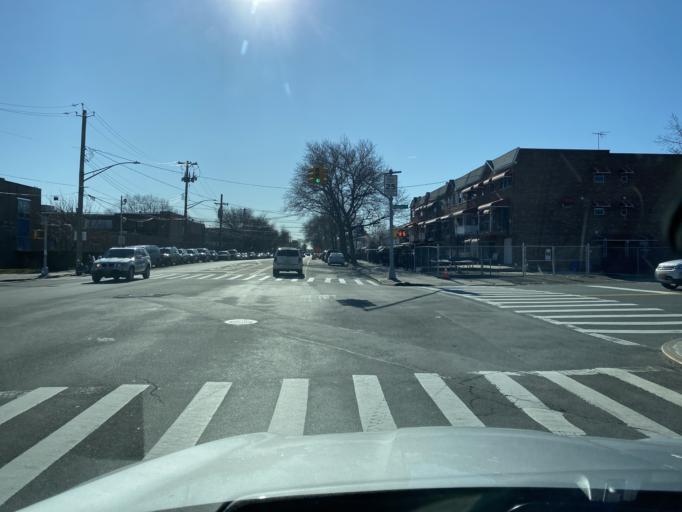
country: US
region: New York
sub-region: Bronx
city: The Bronx
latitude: 40.8179
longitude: -73.8573
